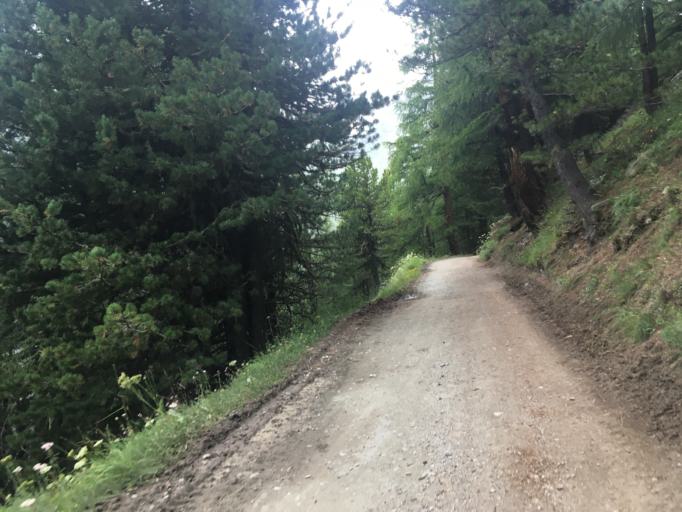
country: CH
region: Valais
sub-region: Visp District
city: Zermatt
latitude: 46.0274
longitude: 7.7754
